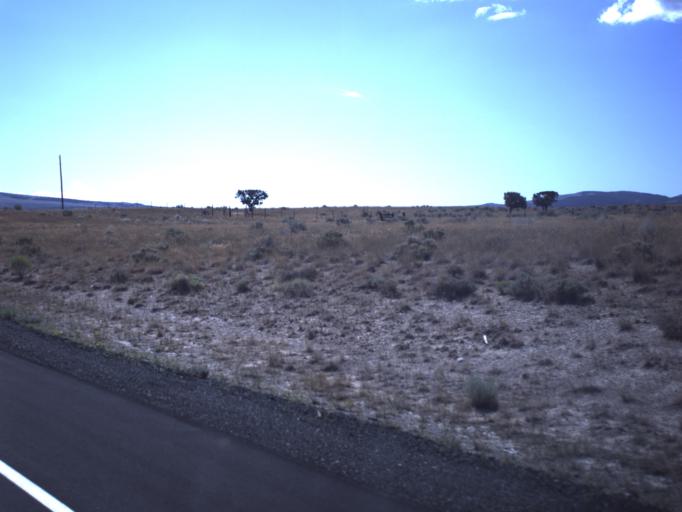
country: US
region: Utah
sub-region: Utah County
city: Eagle Mountain
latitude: 40.0600
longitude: -112.3114
